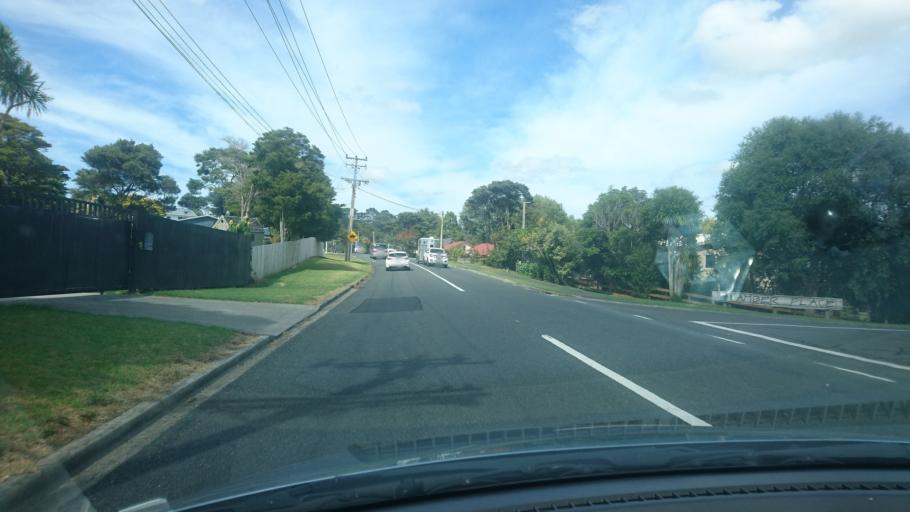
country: NZ
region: Auckland
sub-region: Auckland
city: Muriwai Beach
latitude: -36.7721
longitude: 174.4908
